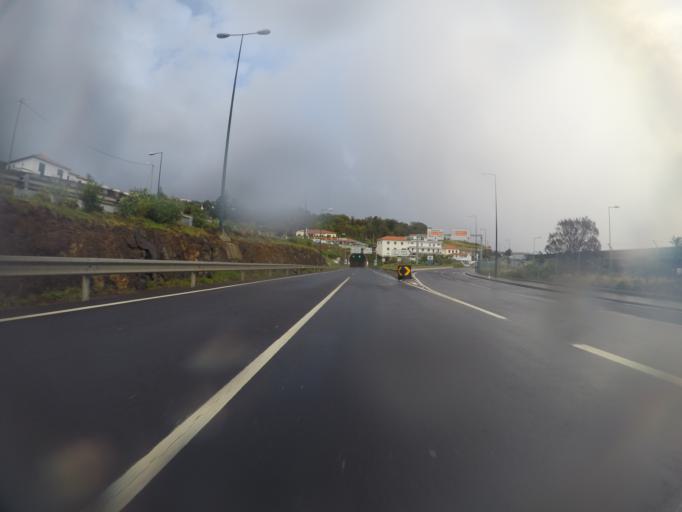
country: PT
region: Madeira
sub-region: Machico
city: Machico
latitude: 32.7064
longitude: -16.7670
